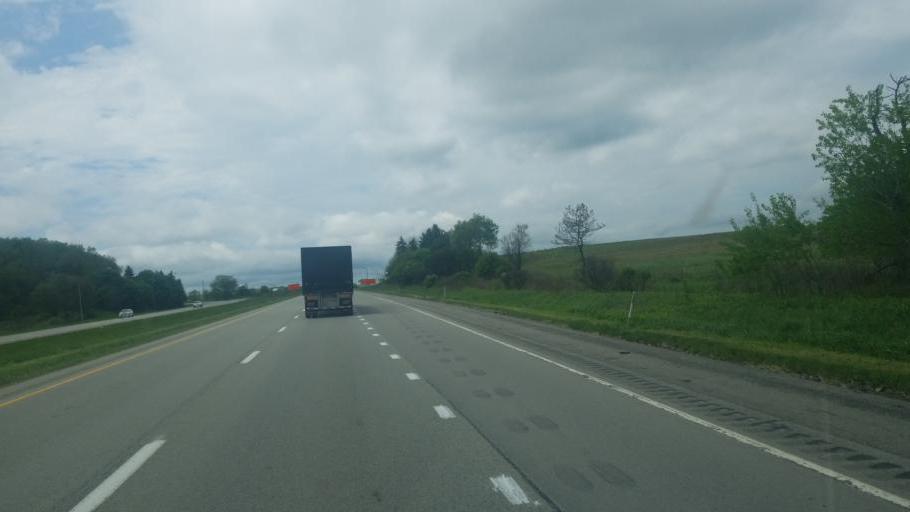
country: US
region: Pennsylvania
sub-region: Mercer County
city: Grove City
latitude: 41.2011
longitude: -80.0654
